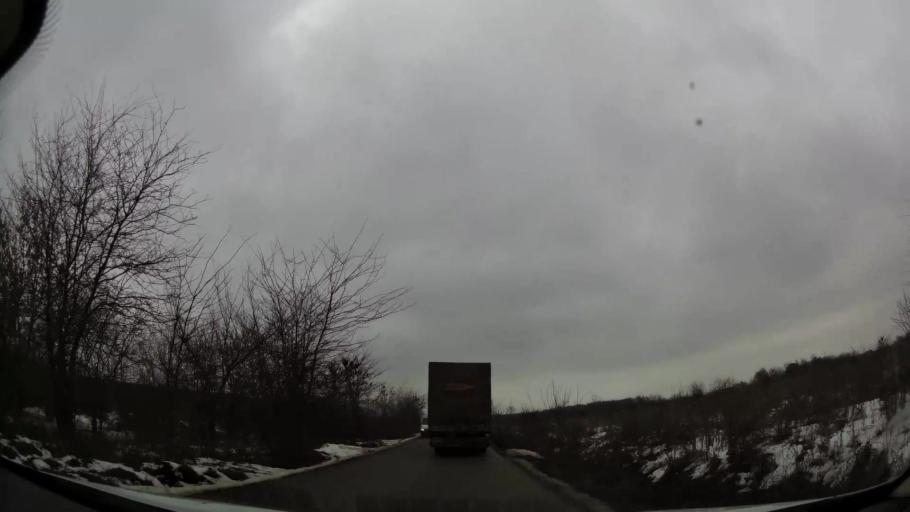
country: RO
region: Ilfov
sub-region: Comuna Chitila
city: Chitila
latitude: 44.5008
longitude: 26.0071
